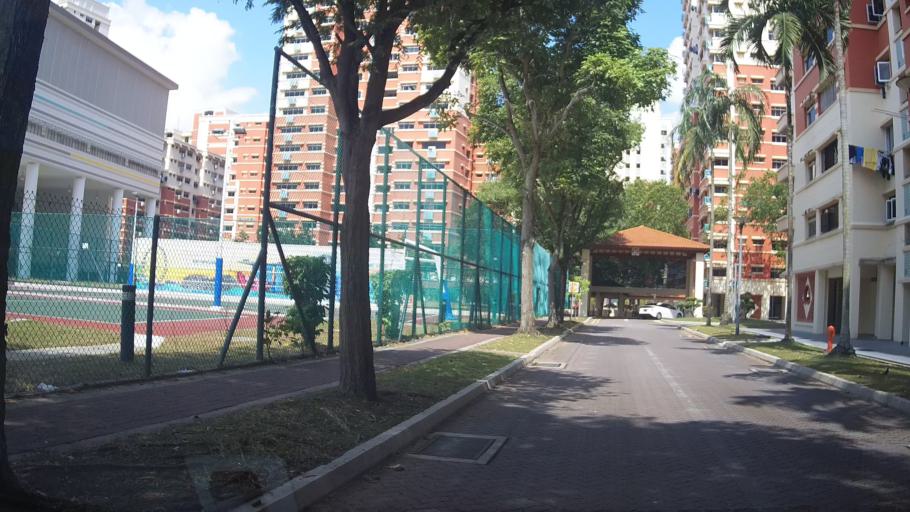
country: MY
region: Johor
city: Kampung Pasir Gudang Baru
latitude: 1.3754
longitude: 103.9457
